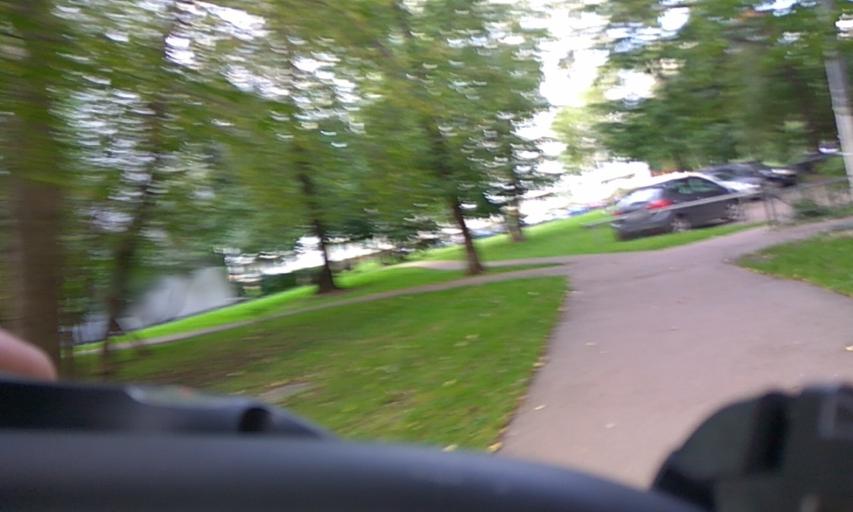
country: RU
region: Moscow
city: Kolomenskoye
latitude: 55.6876
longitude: 37.6887
